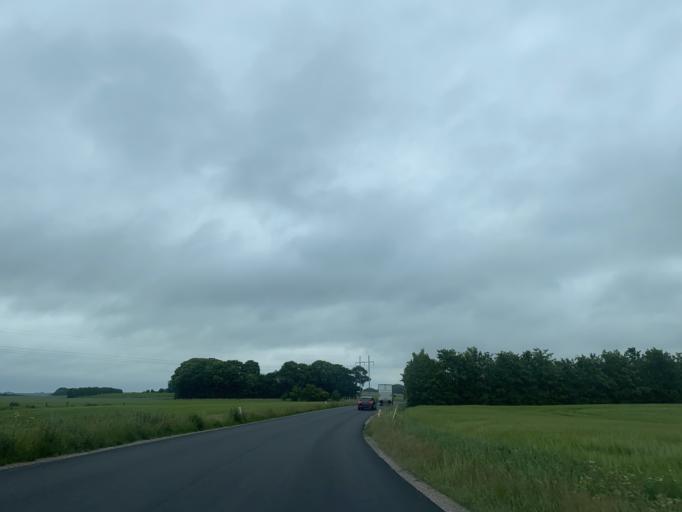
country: DK
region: Central Jutland
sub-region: Viborg Kommune
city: Bjerringbro
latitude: 56.3075
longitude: 9.7290
